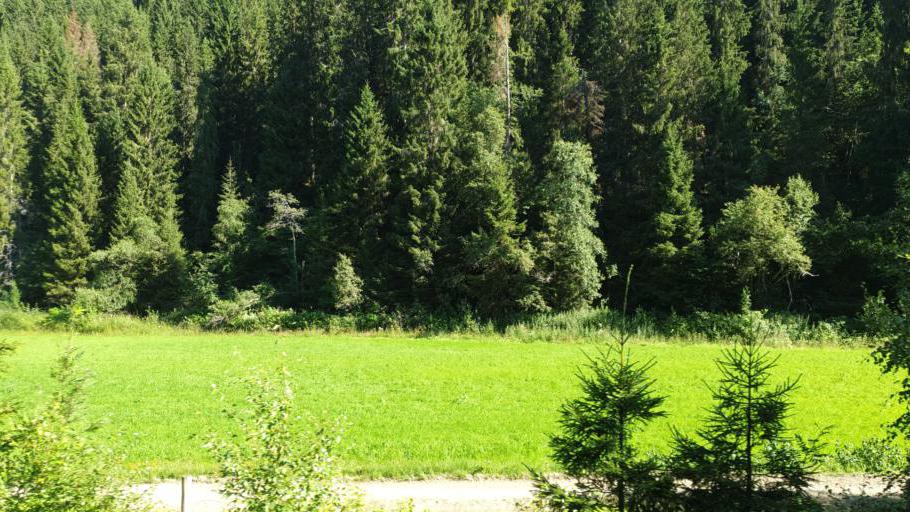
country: NO
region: Sor-Trondelag
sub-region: Orkdal
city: Orkanger
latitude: 63.1918
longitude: 9.7824
